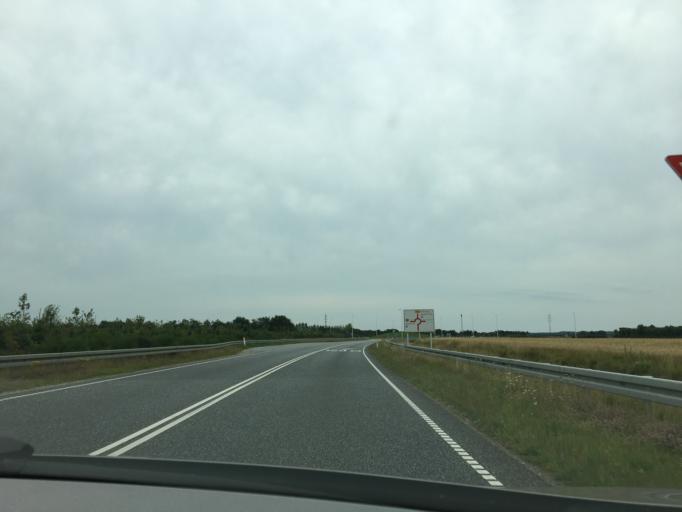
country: DK
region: Central Jutland
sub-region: Herning Kommune
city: Sunds
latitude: 56.2222
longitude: 9.0090
